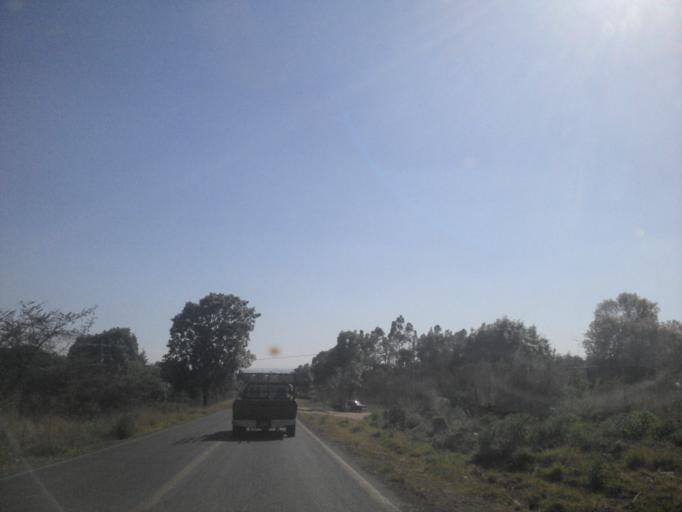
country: MX
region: Jalisco
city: Arandas
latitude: 20.7495
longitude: -102.3083
